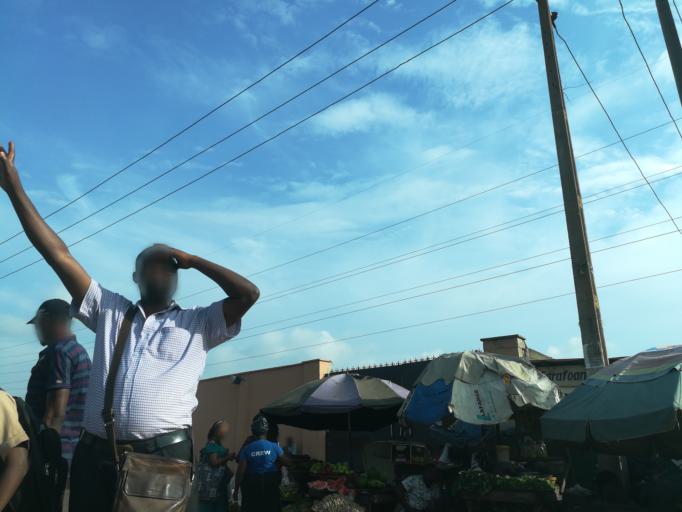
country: NG
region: Lagos
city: Ojota
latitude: 6.6093
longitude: 3.4227
